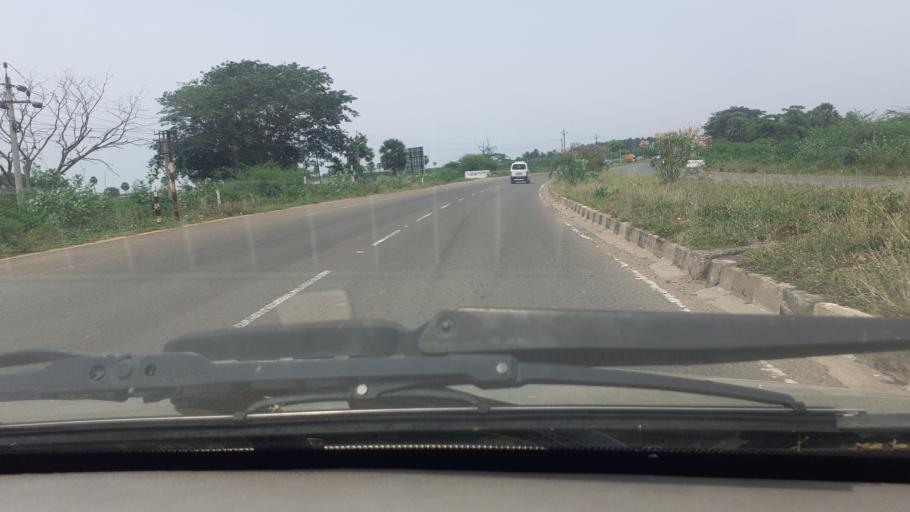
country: IN
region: Tamil Nadu
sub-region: Thoothukkudi
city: Srivaikuntam
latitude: 8.7365
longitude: 77.9020
